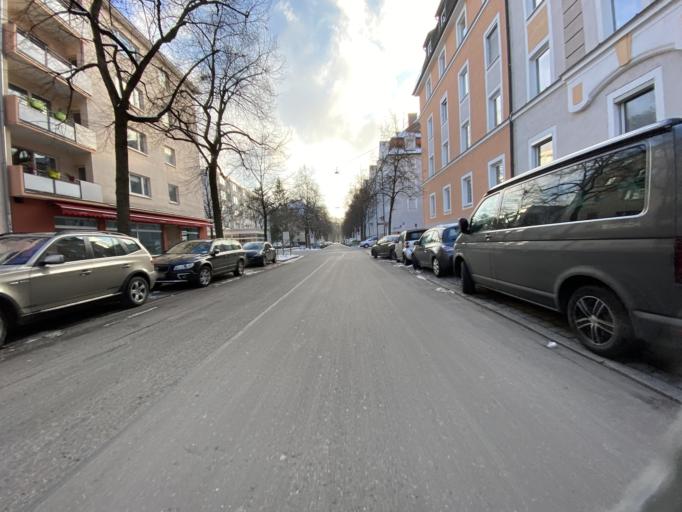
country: DE
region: Bavaria
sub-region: Upper Bavaria
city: Munich
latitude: 48.1187
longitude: 11.5453
